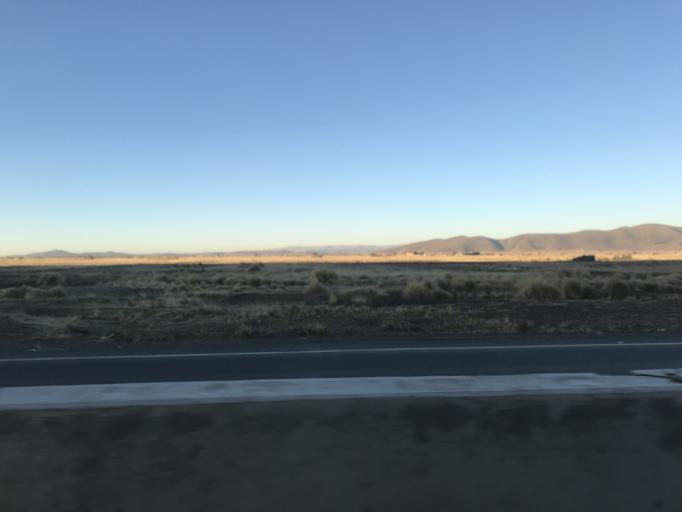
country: BO
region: La Paz
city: Batallas
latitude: -16.2987
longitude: -68.5188
